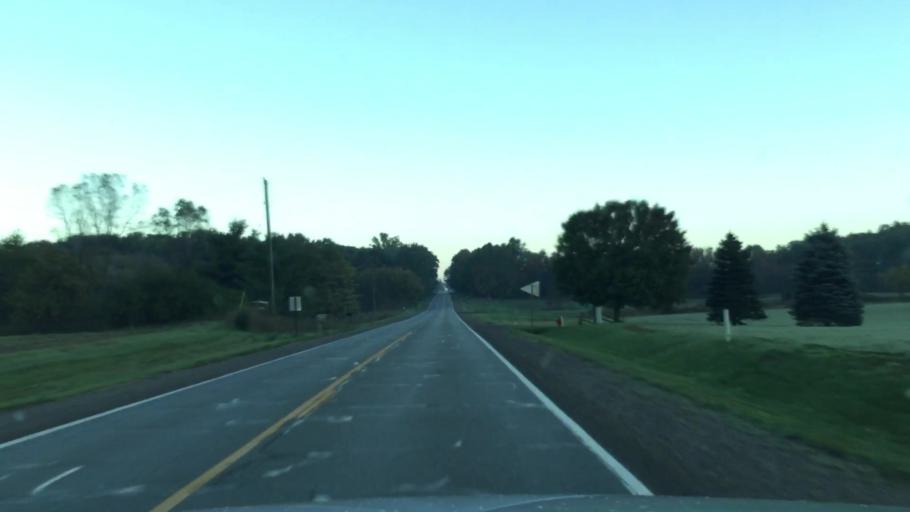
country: US
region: Michigan
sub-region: Livingston County
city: Howell
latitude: 42.6543
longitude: -83.9354
